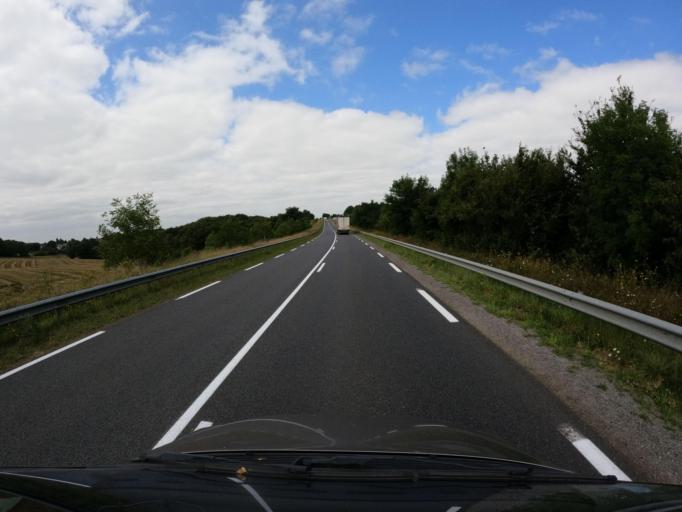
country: FR
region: Poitou-Charentes
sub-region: Departement de la Vienne
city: Charroux
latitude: 46.1481
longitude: 0.4121
